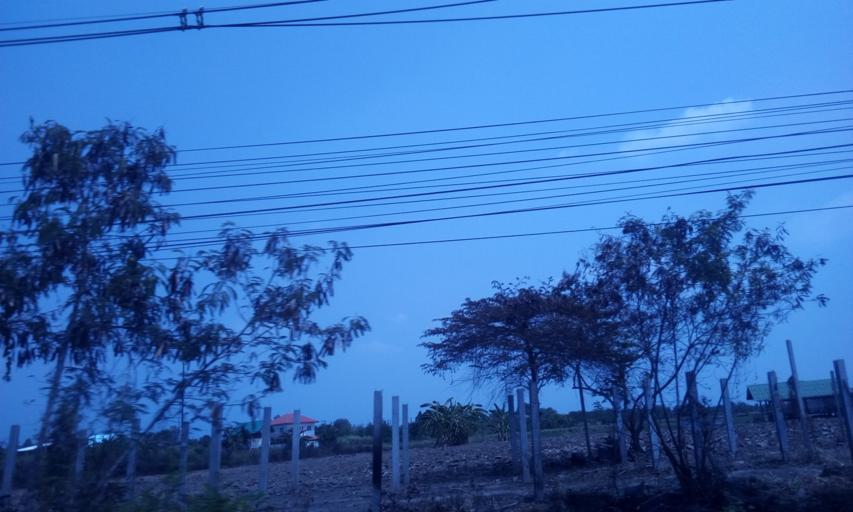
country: TH
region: Chachoengsao
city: Chachoengsao
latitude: 13.7564
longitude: 101.0749
